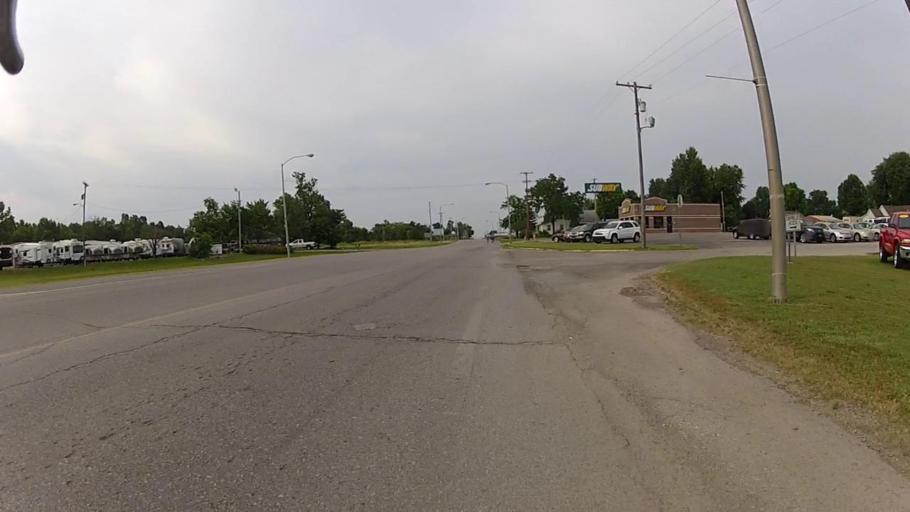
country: US
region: Kansas
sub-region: Cherokee County
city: Columbus
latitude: 37.1775
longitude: -94.8318
